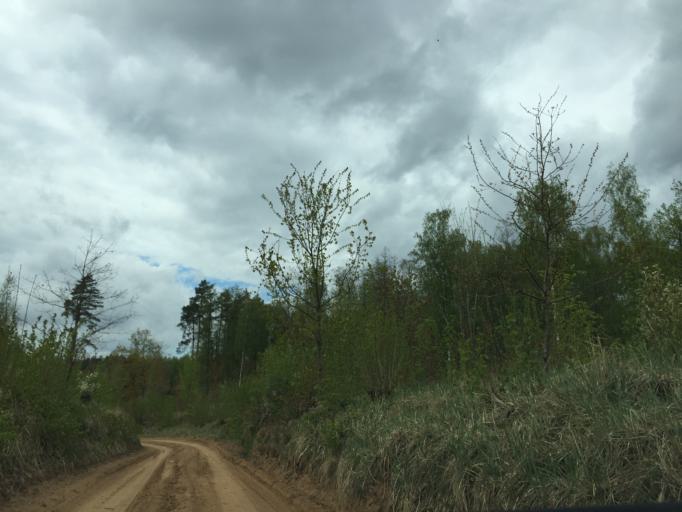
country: LV
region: Kekava
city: Kekava
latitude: 56.8008
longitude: 24.3015
